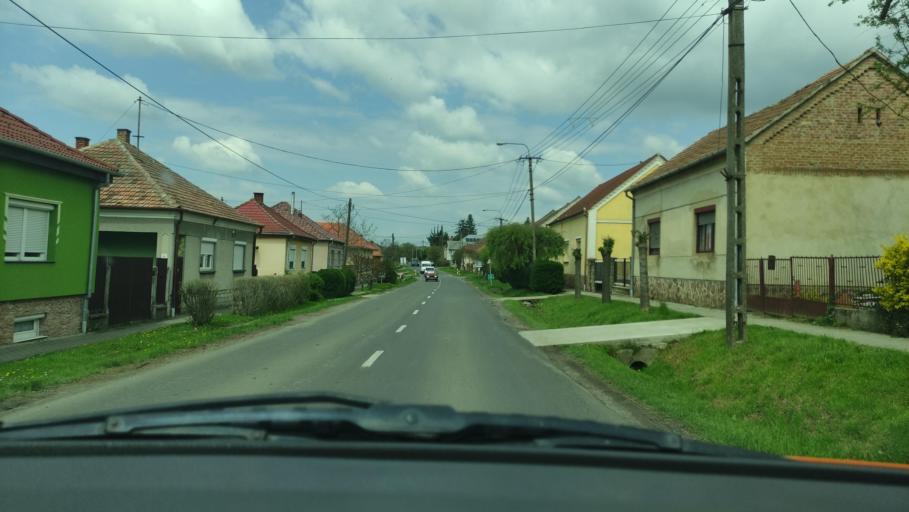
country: HU
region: Baranya
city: Sasd
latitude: 46.2585
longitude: 18.0972
